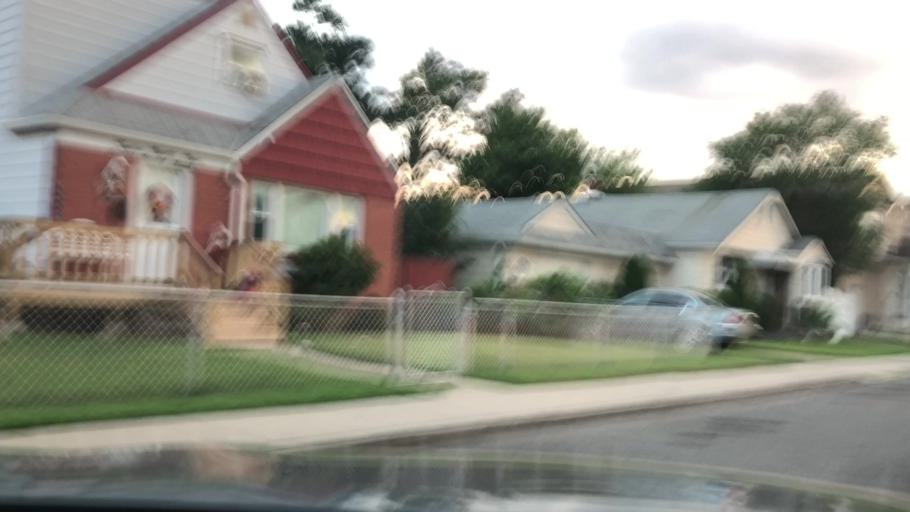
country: US
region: New York
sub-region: Nassau County
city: Franklin Square
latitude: 40.7041
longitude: -73.6888
